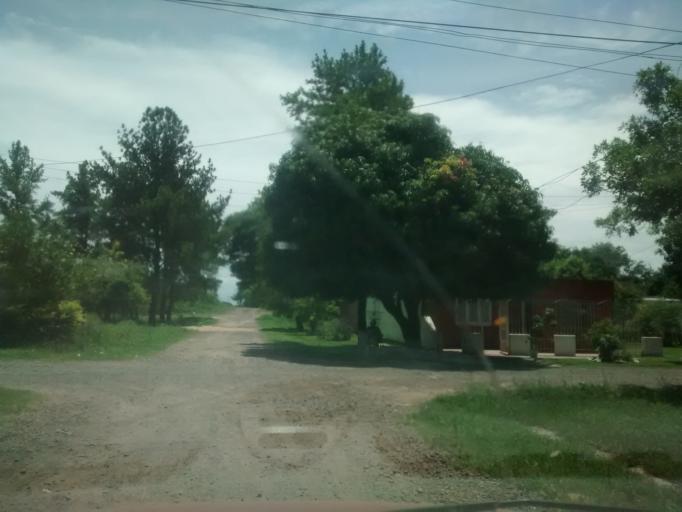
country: AR
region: Chaco
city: Resistencia
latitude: -27.4330
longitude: -58.9757
